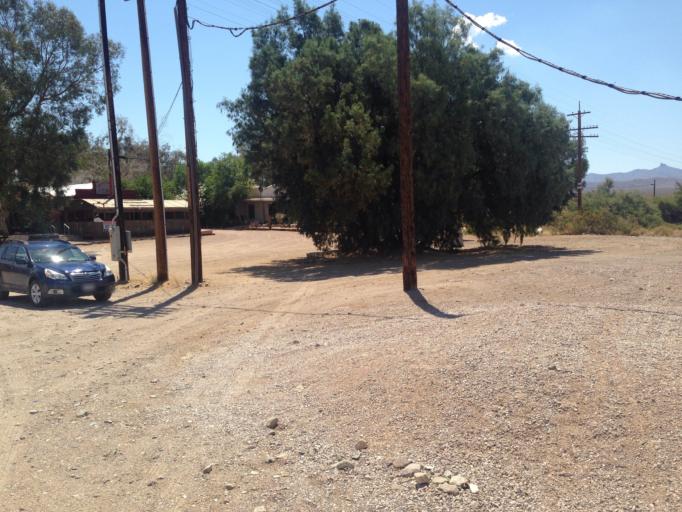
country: US
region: Nevada
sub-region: Clark County
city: Sandy Valley
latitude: 35.4670
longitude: -115.2726
